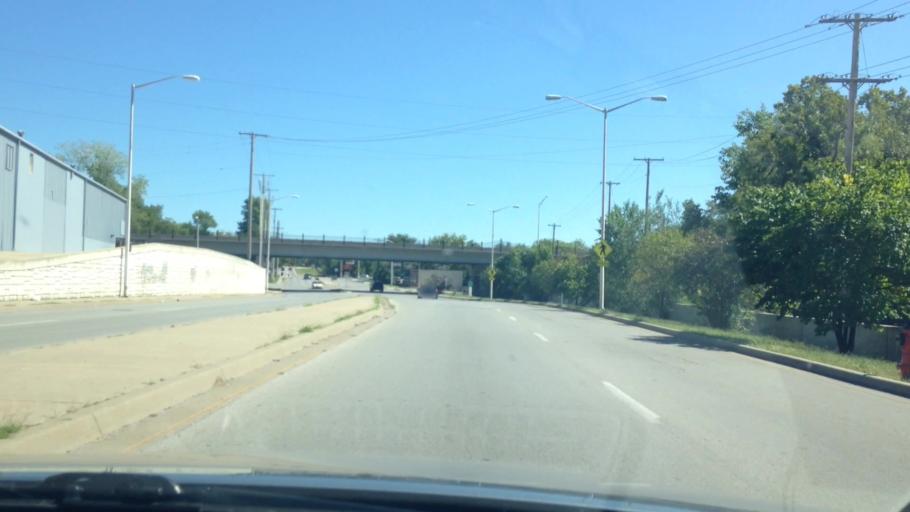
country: US
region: Kansas
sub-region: Johnson County
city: Leawood
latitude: 38.9736
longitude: -94.5783
